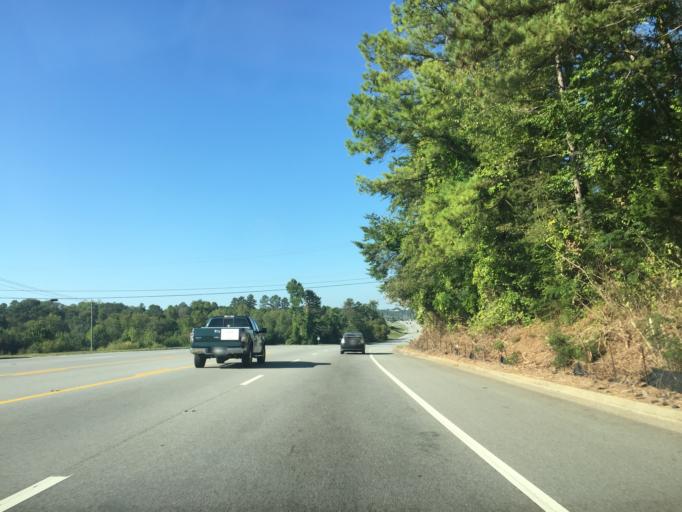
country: US
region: Tennessee
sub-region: Hamilton County
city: Harrison
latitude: 35.1142
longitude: -85.1303
